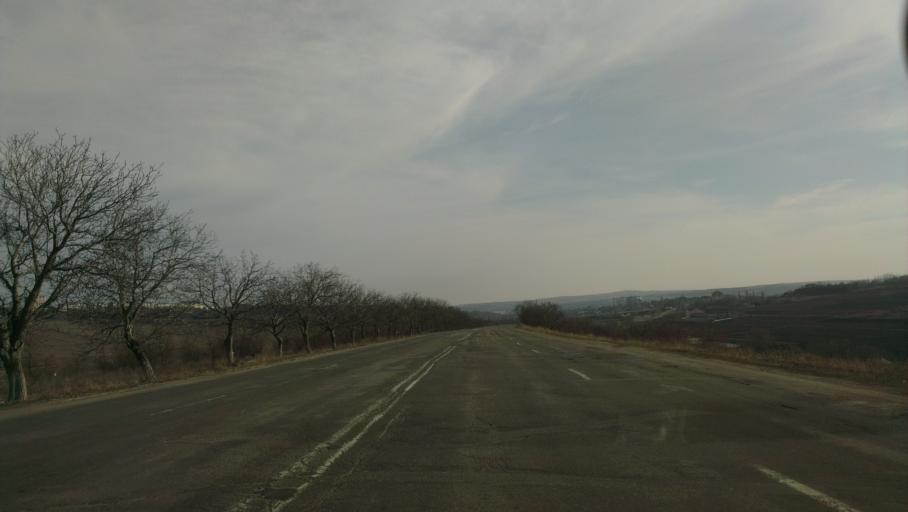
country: MD
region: Laloveni
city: Ialoveni
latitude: 46.9770
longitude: 28.7491
